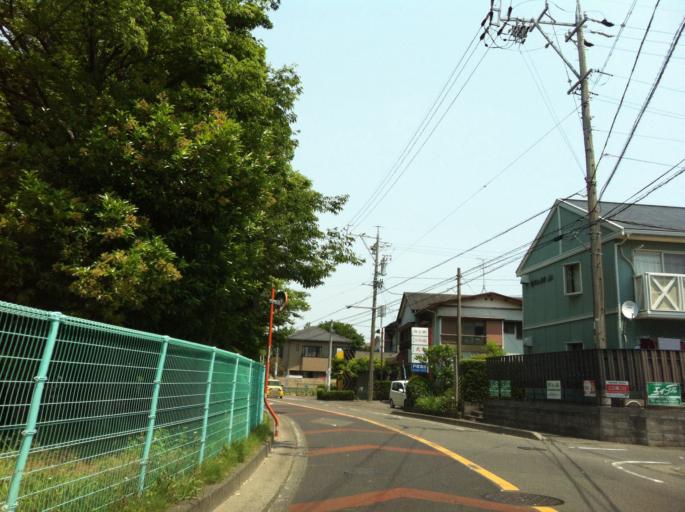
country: JP
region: Shizuoka
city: Shizuoka-shi
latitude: 34.9868
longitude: 138.4306
